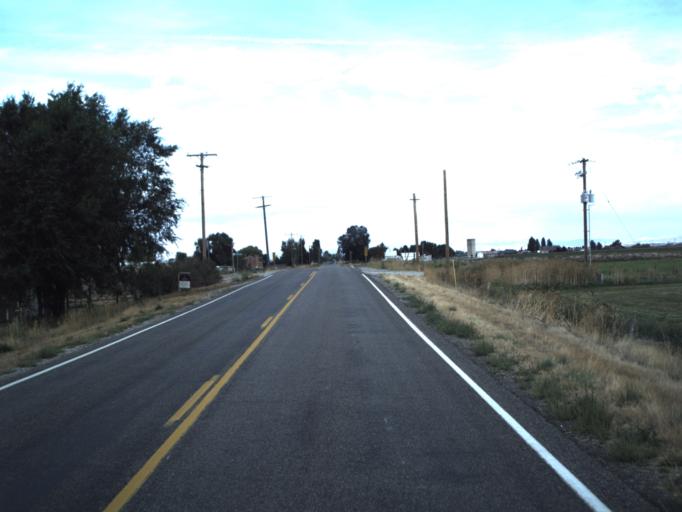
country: US
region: Utah
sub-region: Cache County
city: Lewiston
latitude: 41.9315
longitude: -111.9532
